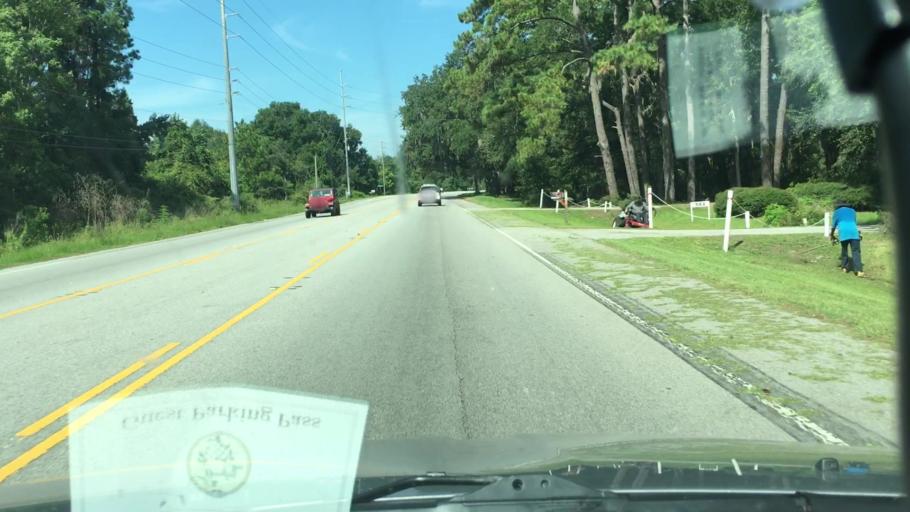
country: US
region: South Carolina
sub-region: Beaufort County
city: Beaufort
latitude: 32.3972
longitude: -80.6031
